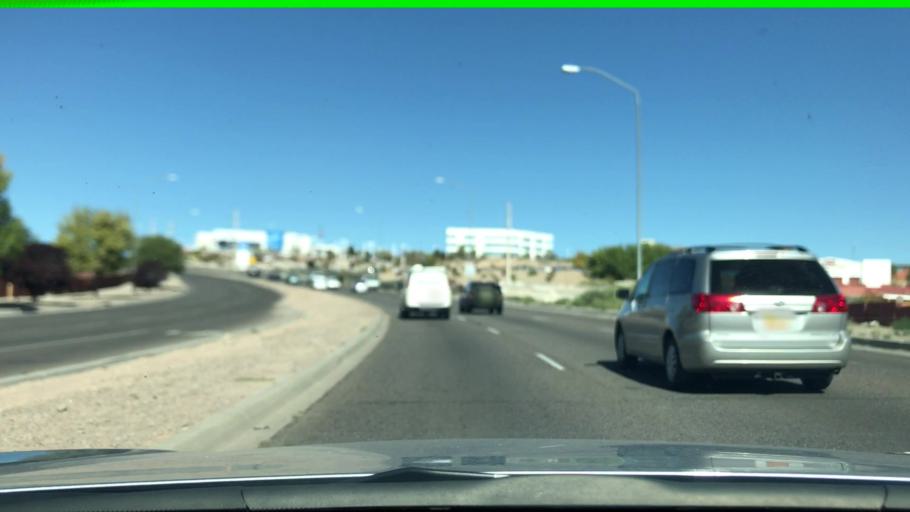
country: US
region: New Mexico
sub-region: Sandoval County
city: Rio Rancho
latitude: 35.2097
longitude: -106.6587
